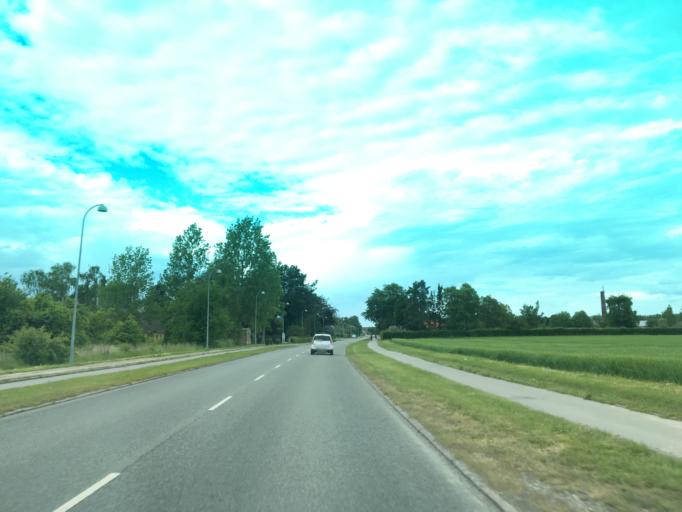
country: DK
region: Capital Region
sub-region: Hvidovre Kommune
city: Hvidovre
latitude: 55.6363
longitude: 12.4496
